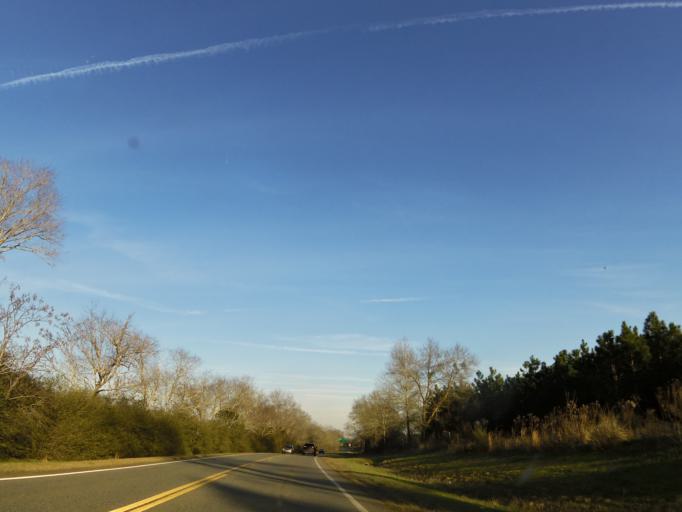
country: US
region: Georgia
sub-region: Sumter County
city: Americus
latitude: 32.0476
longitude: -84.3509
